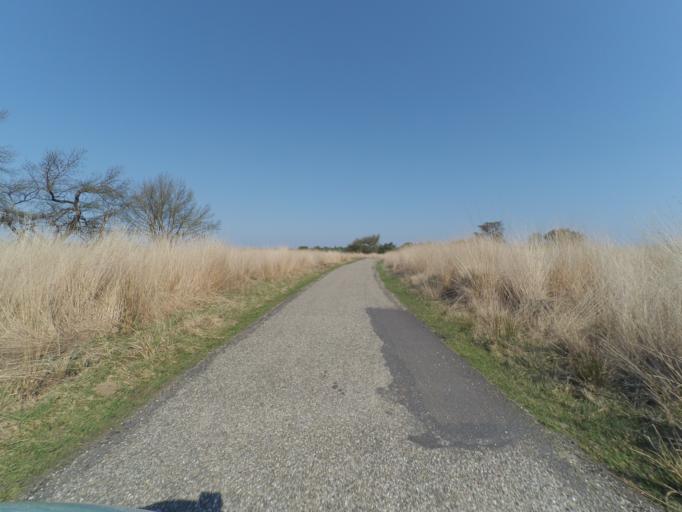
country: NL
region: Gelderland
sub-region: Gemeente Ede
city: Otterlo
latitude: 52.0883
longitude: 5.8522
